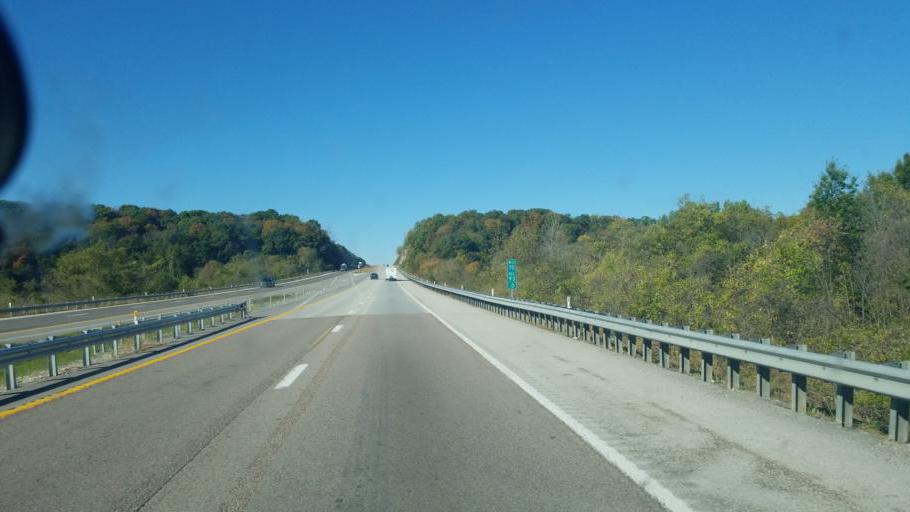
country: US
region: Missouri
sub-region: Cooper County
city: Boonville
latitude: 38.9340
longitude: -92.9434
